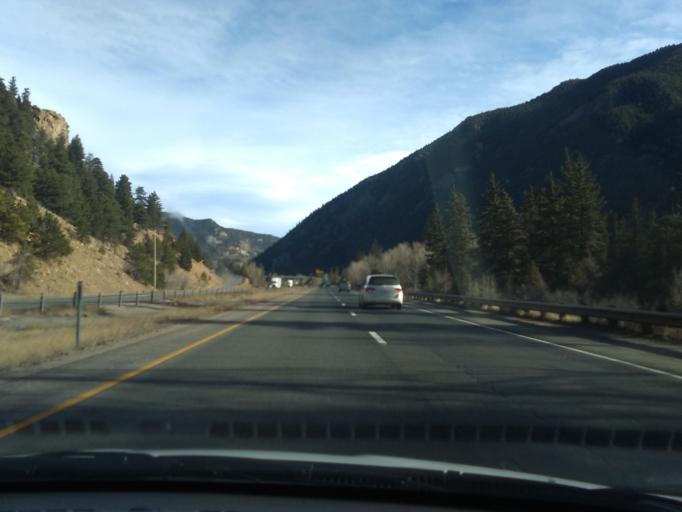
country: US
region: Colorado
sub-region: Clear Creek County
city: Georgetown
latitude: 39.7501
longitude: -105.6665
